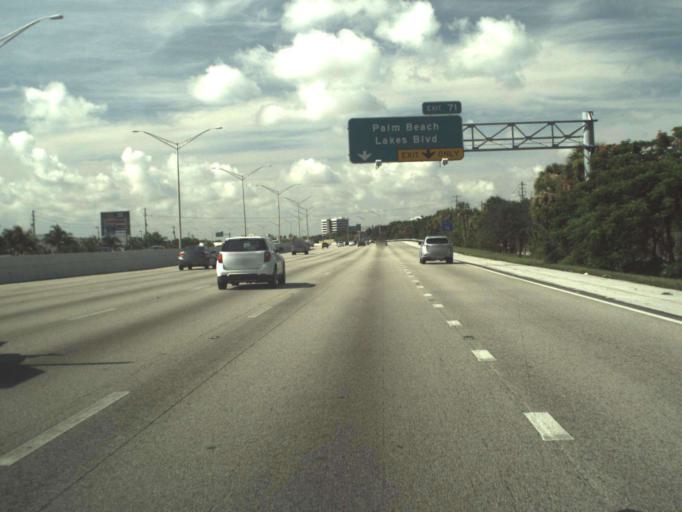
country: US
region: Florida
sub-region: Palm Beach County
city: Schall Circle
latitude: 26.7276
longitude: -80.0916
